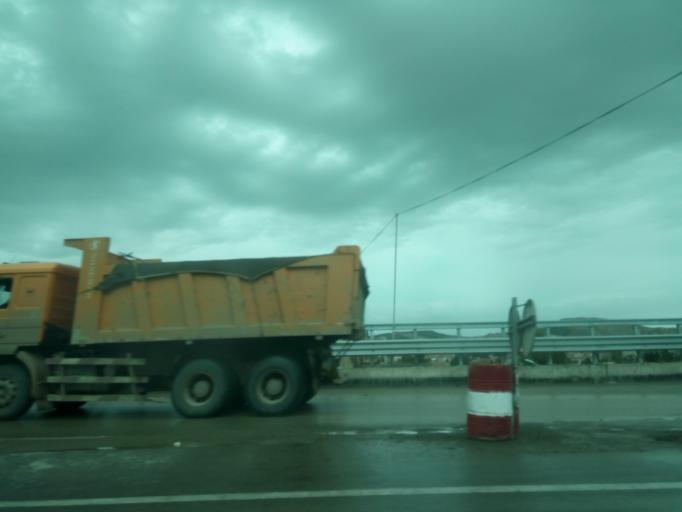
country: DZ
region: Medea
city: Ksar el Boukhari
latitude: 35.8851
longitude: 2.7353
